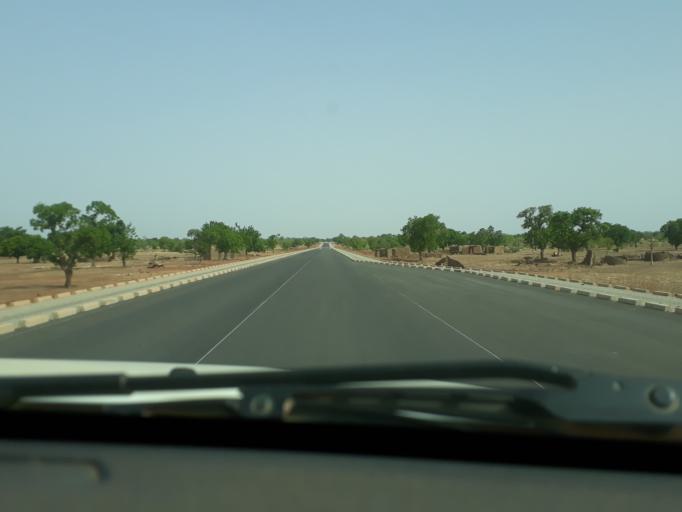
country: BF
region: Plateau-Central
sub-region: Province d'Oubritenga
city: Ziniare
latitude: 12.5654
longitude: -1.4590
